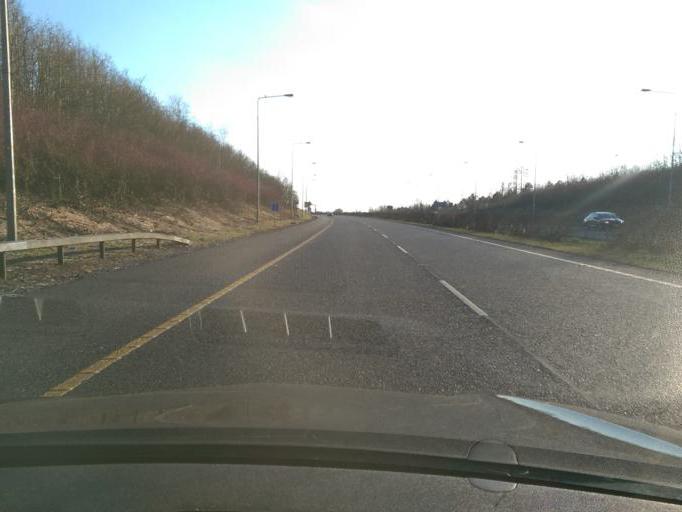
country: IE
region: Leinster
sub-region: Laois
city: Portlaoise
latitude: 53.0502
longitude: -7.2392
